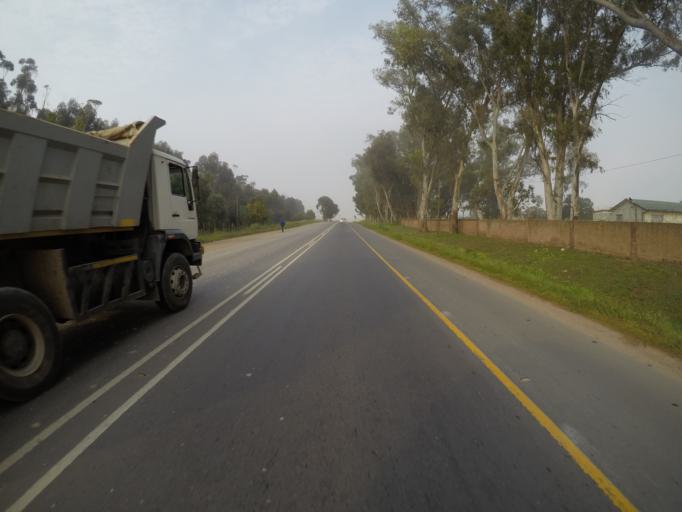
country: ZA
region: Western Cape
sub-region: City of Cape Town
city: Kraaifontein
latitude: -33.7943
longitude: 18.6944
